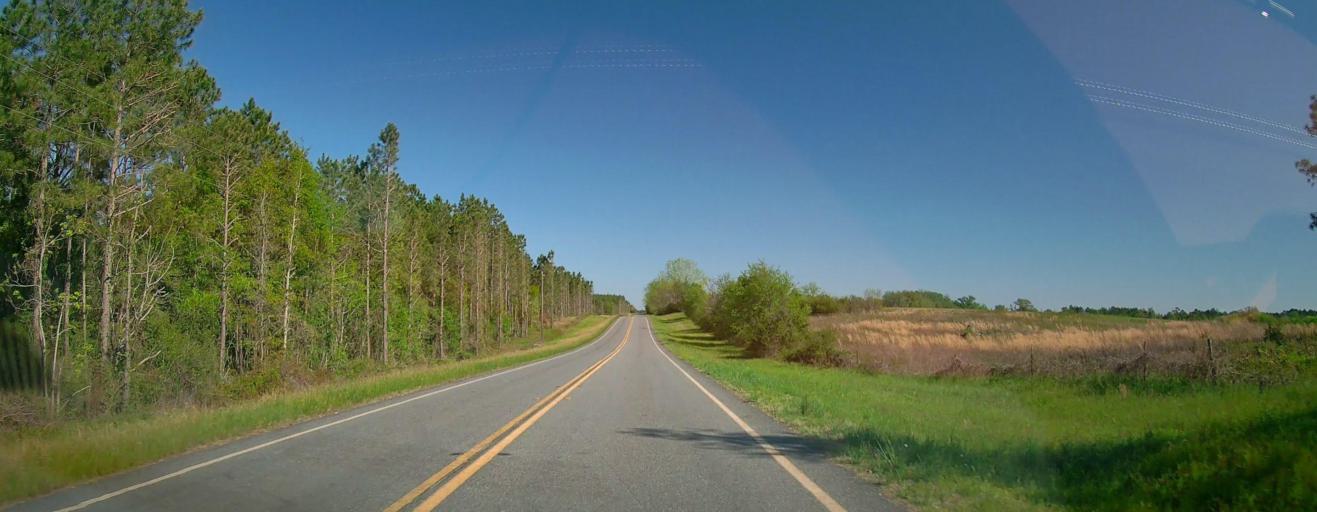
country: US
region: Georgia
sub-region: Wilcox County
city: Rochelle
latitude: 32.0012
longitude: -83.4804
